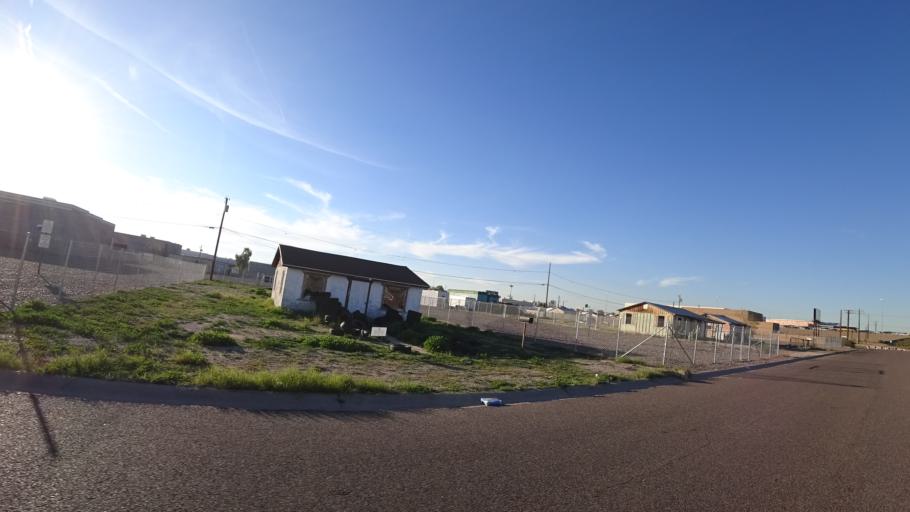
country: US
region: Arizona
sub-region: Maricopa County
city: Phoenix
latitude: 33.4246
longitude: -112.0435
